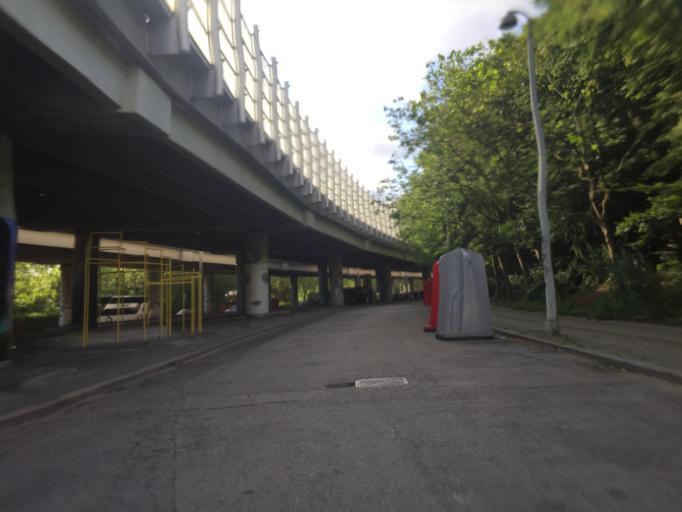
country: DK
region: Capital Region
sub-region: Frederiksberg Kommune
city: Frederiksberg
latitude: 55.6949
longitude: 12.5344
